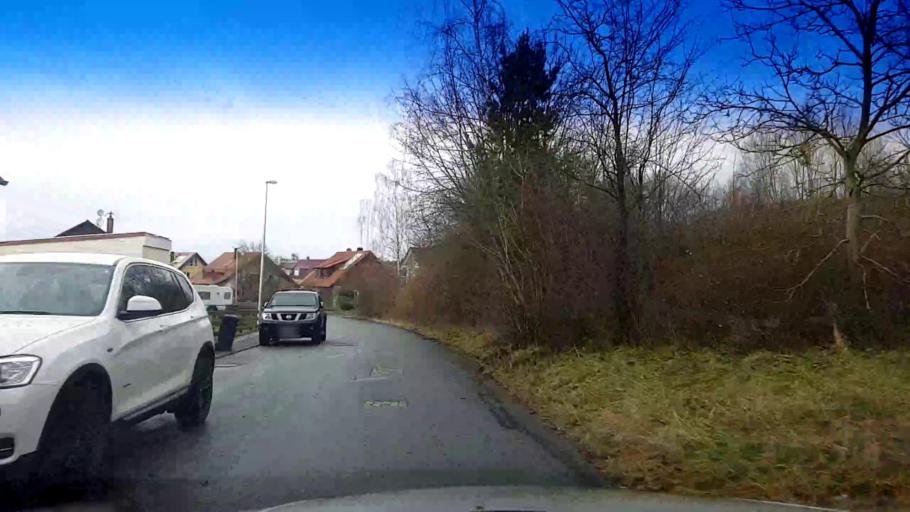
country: DE
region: Bavaria
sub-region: Upper Franconia
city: Litzendorf
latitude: 49.9261
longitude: 11.0094
